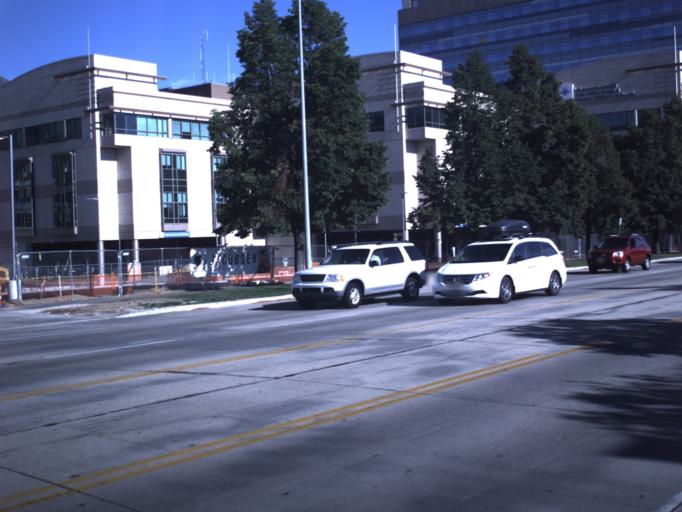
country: US
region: Utah
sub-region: Utah County
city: Provo
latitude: 40.2493
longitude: -111.6675
